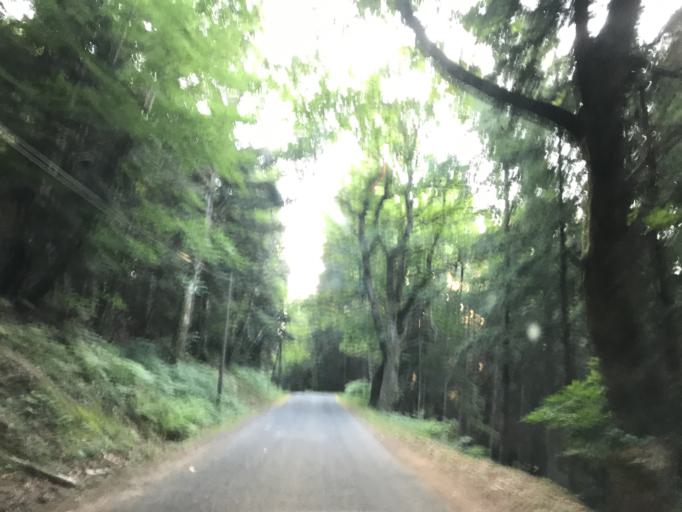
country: FR
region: Auvergne
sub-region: Departement du Puy-de-Dome
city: Celles-sur-Durolle
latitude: 45.7547
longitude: 3.6498
